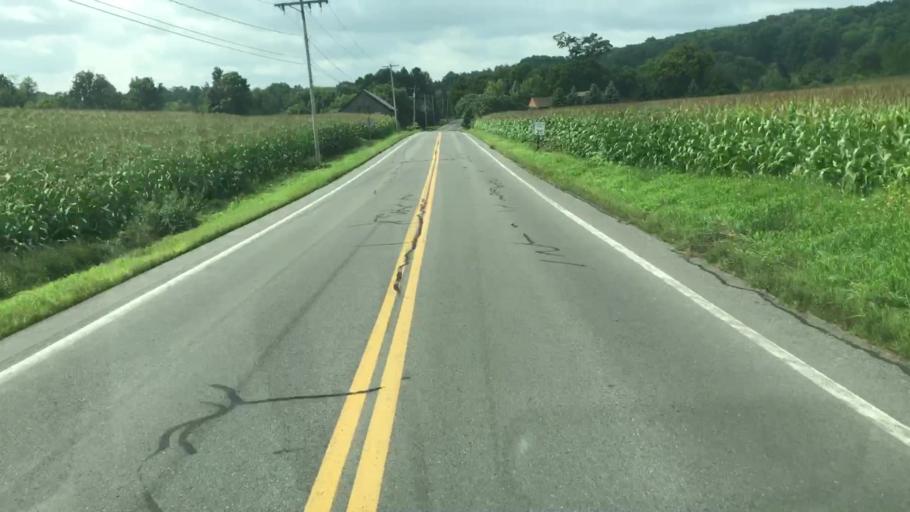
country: US
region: New York
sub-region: Onondaga County
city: Peru
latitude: 43.0608
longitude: -76.3638
